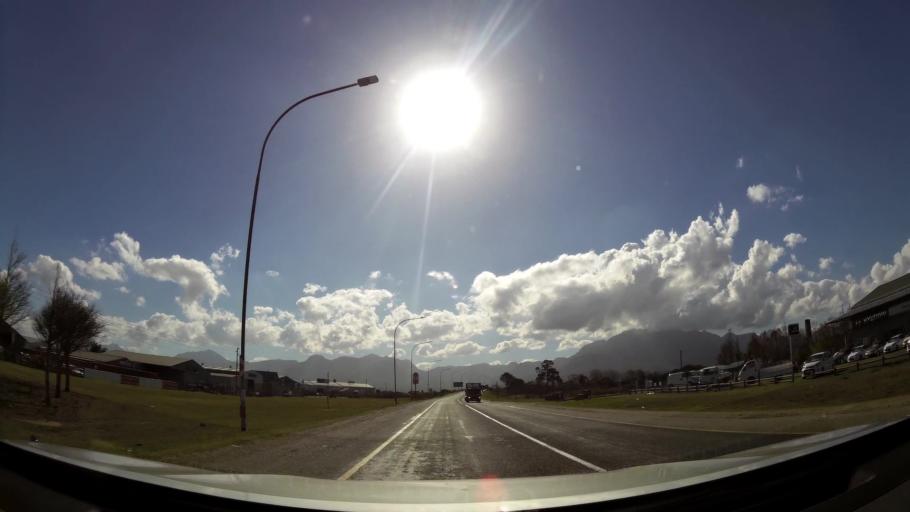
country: ZA
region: Western Cape
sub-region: Eden District Municipality
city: George
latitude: -33.9896
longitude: 22.4422
